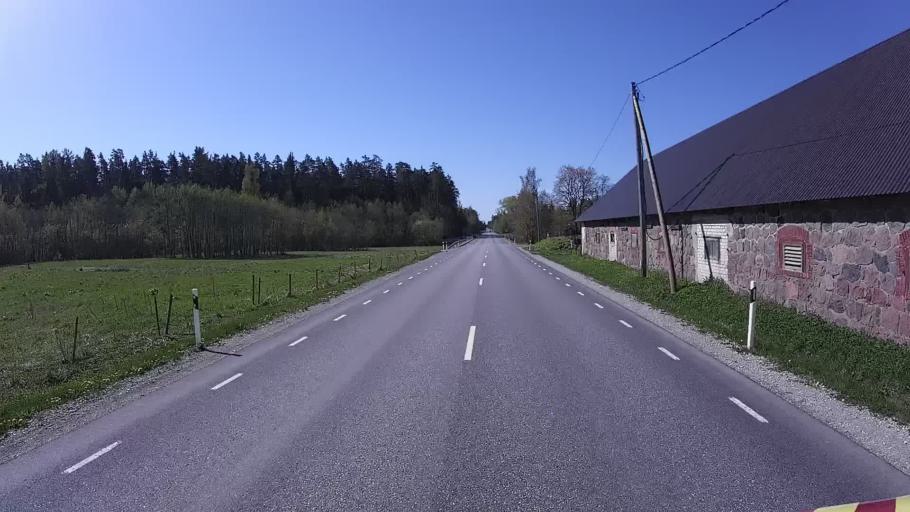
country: EE
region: Raplamaa
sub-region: Jaervakandi vald
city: Jarvakandi
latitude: 58.7333
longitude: 24.8033
